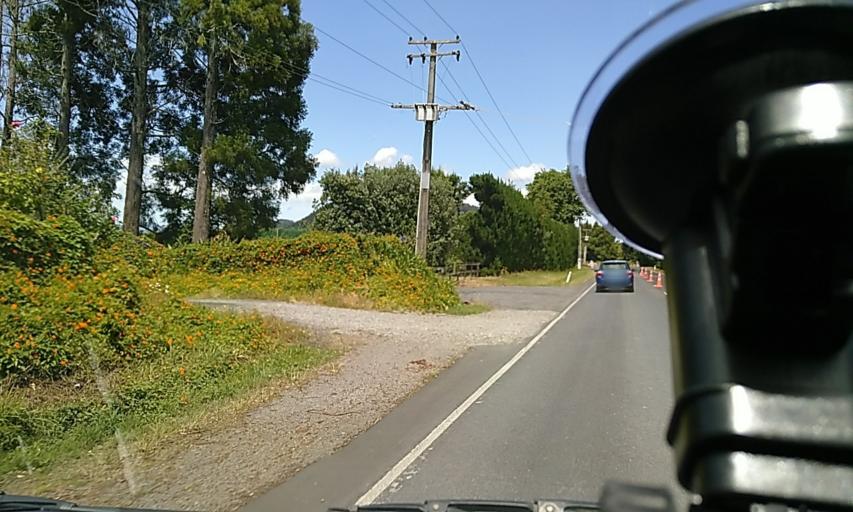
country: NZ
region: Bay of Plenty
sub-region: Western Bay of Plenty District
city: Waihi Beach
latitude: -37.4525
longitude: 175.9446
